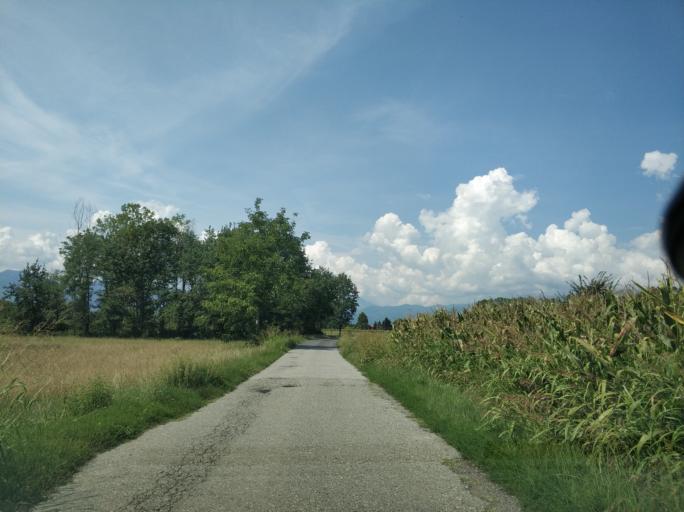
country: IT
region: Piedmont
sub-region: Provincia di Torino
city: San Carlo Canavese
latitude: 45.2361
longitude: 7.6208
